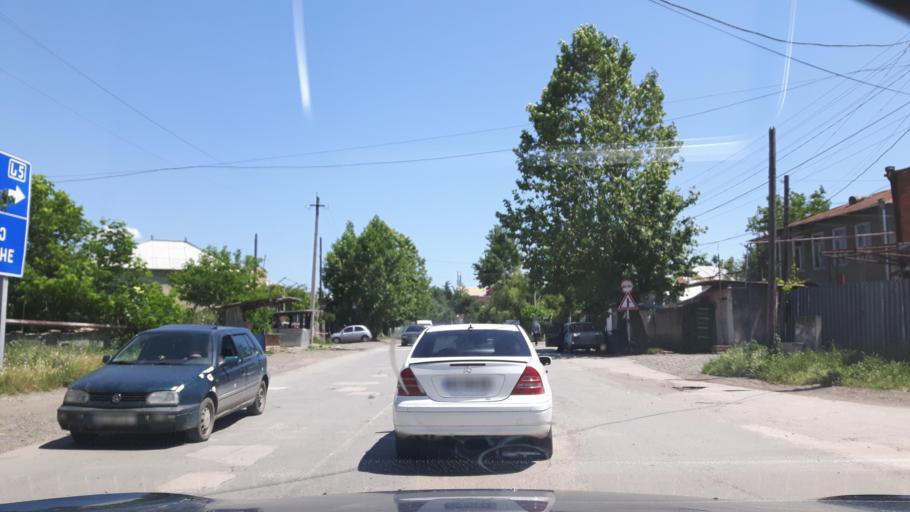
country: GE
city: Tsnori
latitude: 41.6224
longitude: 45.9759
